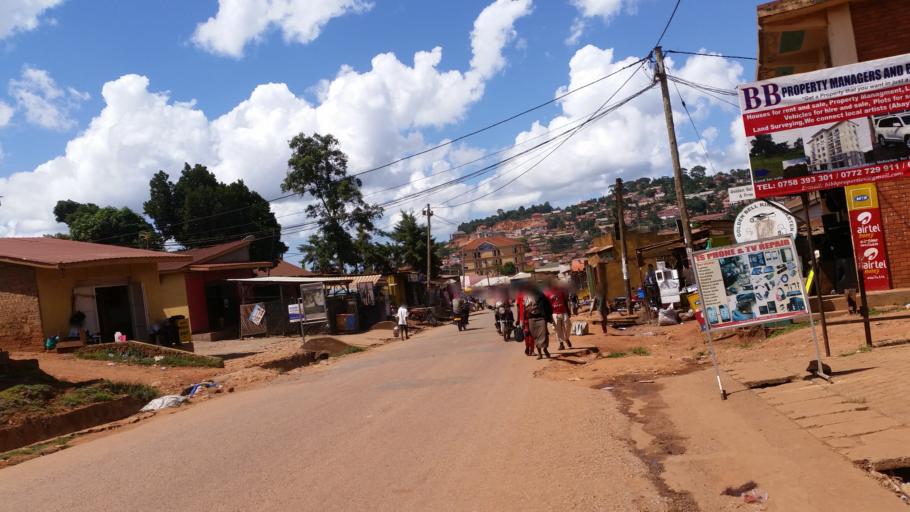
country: UG
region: Central Region
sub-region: Wakiso District
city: Kireka
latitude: 0.3487
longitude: 32.6466
